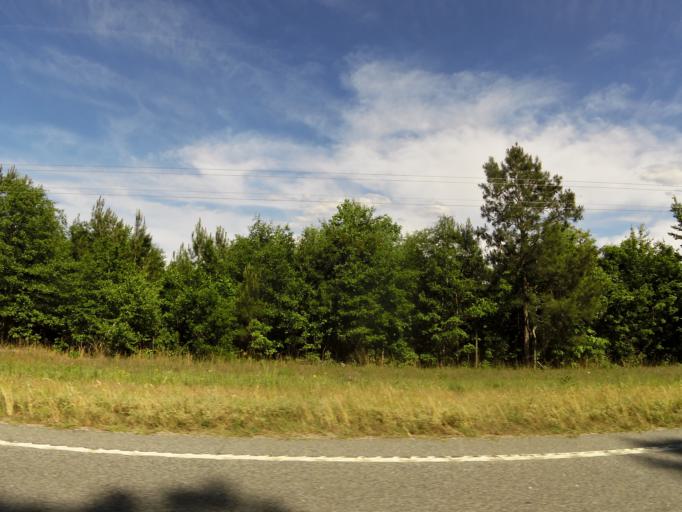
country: US
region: South Carolina
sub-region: Bamberg County
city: Denmark
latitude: 33.2586
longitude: -81.1583
